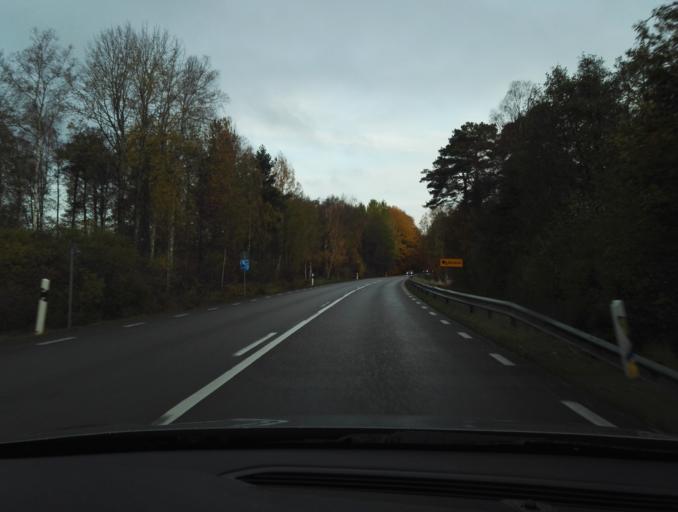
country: SE
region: Kronoberg
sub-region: Vaxjo Kommun
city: Gemla
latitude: 56.9643
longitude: 14.7119
